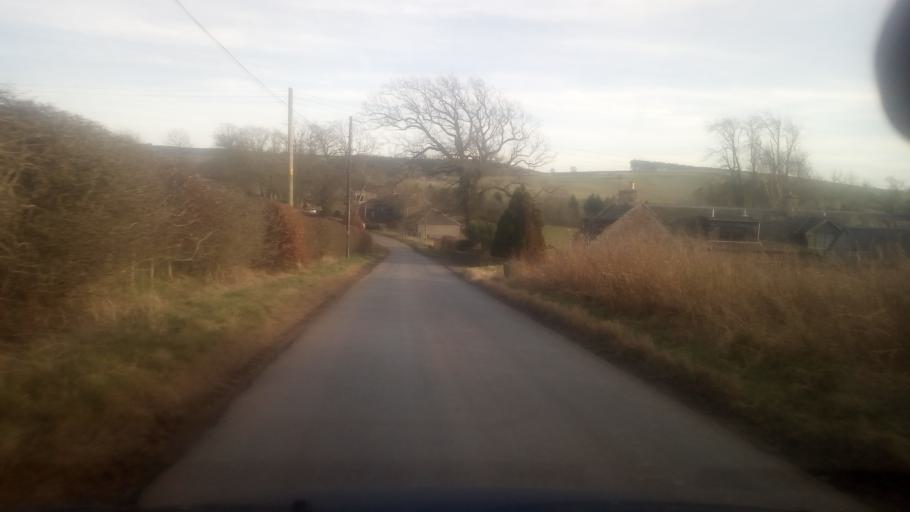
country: GB
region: Scotland
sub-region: The Scottish Borders
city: Jedburgh
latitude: 55.4100
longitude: -2.6100
